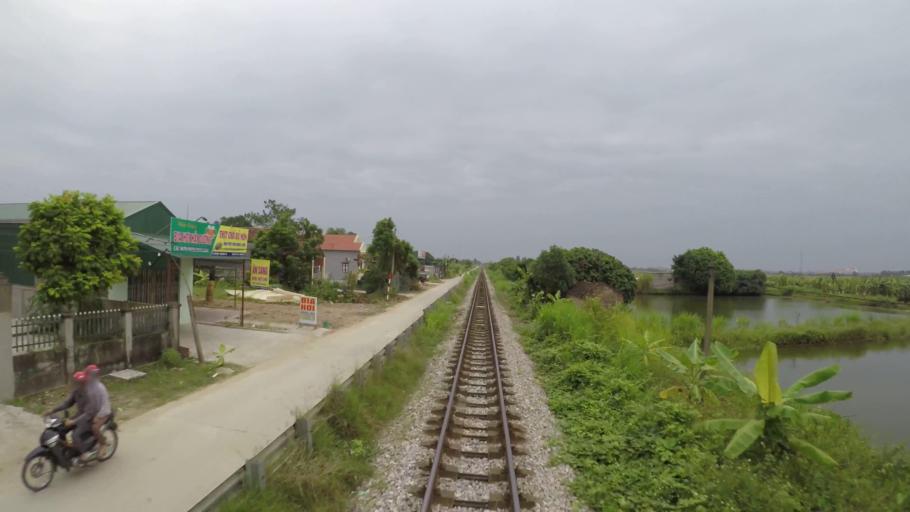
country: VN
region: Hai Duong
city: Lai Cach
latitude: 20.9537
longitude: 106.2243
